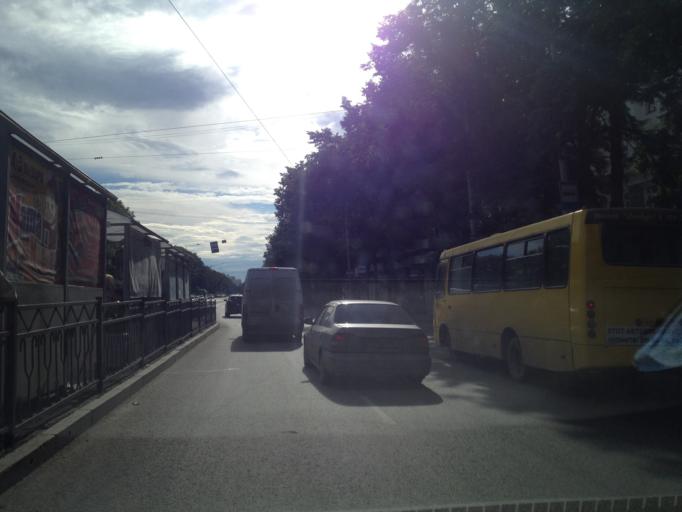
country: RU
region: Sverdlovsk
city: Yekaterinburg
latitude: 56.8432
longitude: 60.6453
